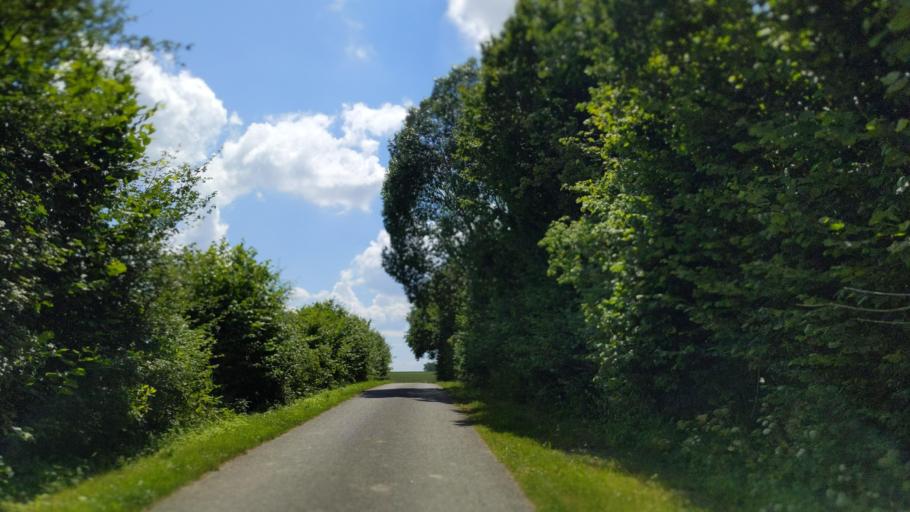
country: DE
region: Schleswig-Holstein
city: Stockelsdorf
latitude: 53.9424
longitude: 10.6489
